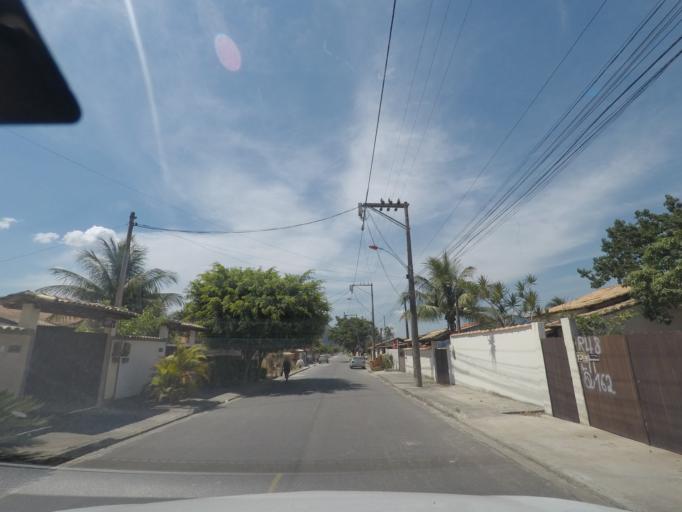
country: BR
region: Rio de Janeiro
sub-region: Marica
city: Marica
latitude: -22.9639
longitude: -42.9576
